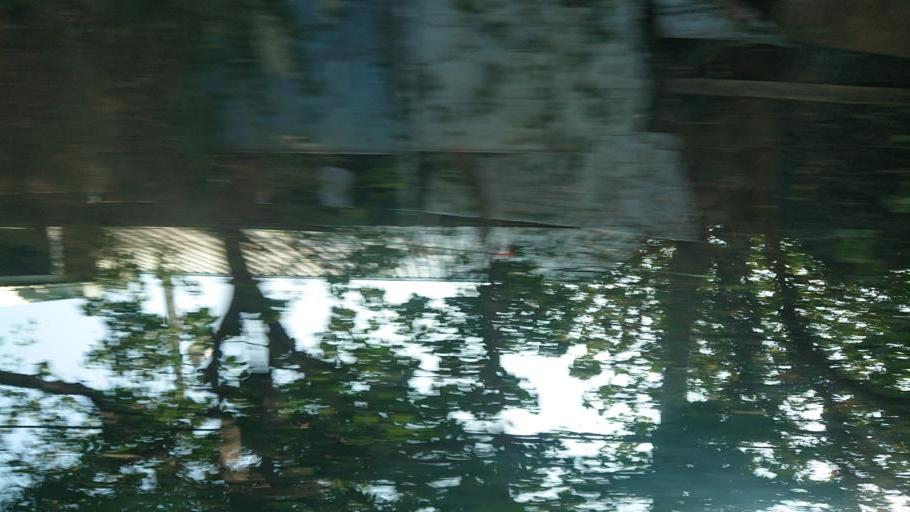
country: TW
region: Taiwan
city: Xinying
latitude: 23.1546
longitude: 120.2493
